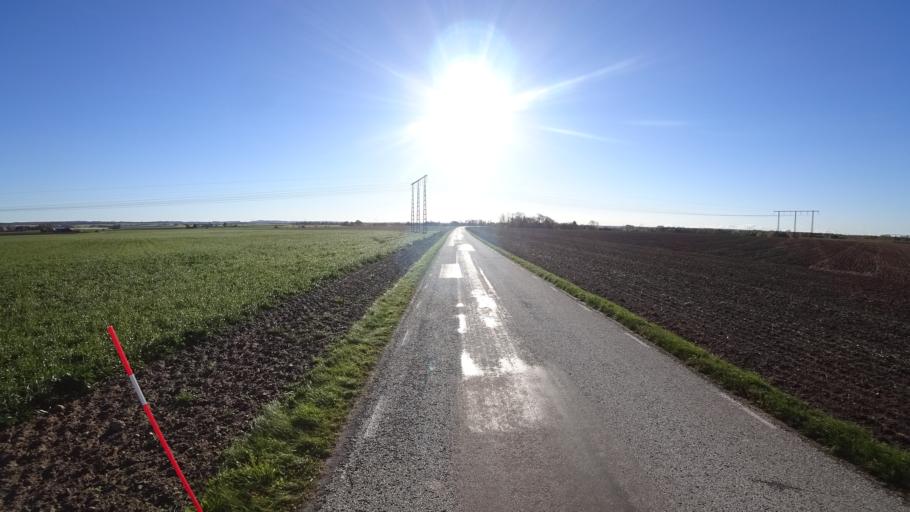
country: SE
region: Skane
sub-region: Staffanstorps Kommun
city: Staffanstorp
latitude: 55.6765
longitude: 13.2296
